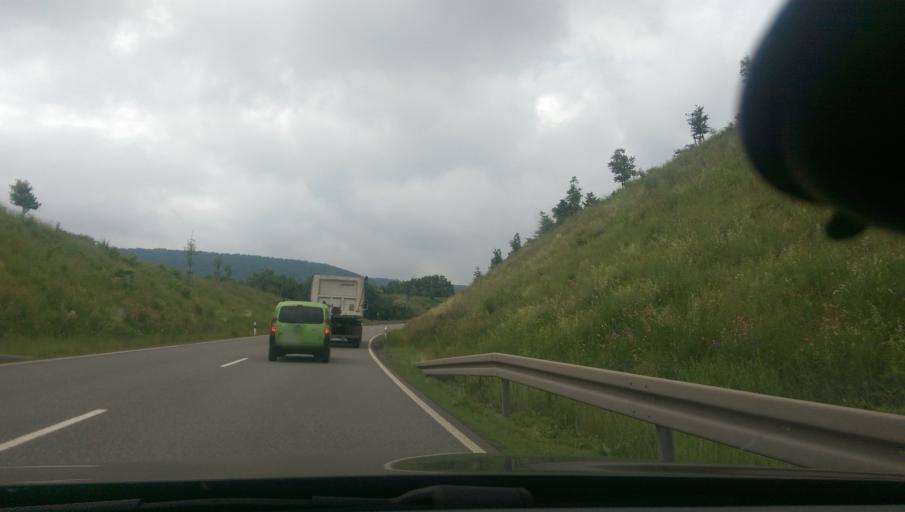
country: DE
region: Thuringia
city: Sondershausen
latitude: 51.3748
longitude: 10.8496
